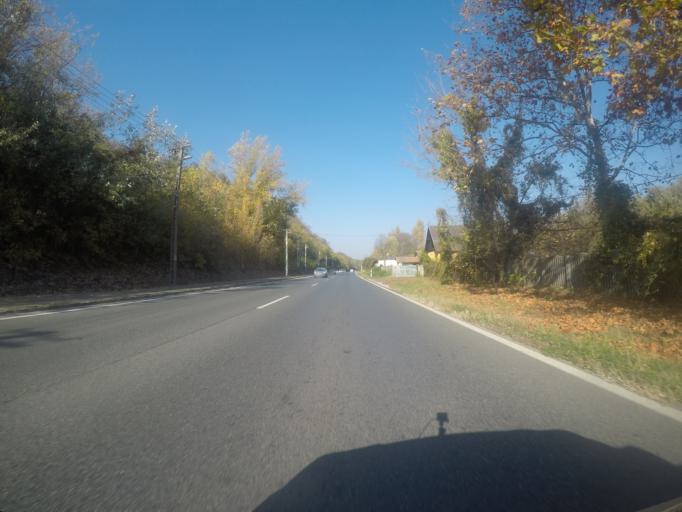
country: HU
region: Tolna
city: Paks
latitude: 46.6399
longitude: 18.8784
